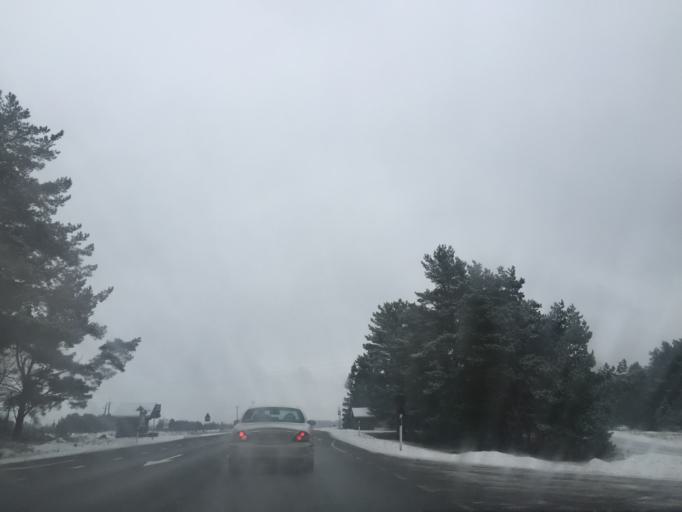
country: EE
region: Laeaene
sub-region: Lihula vald
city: Lihula
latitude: 58.6629
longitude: 23.7322
